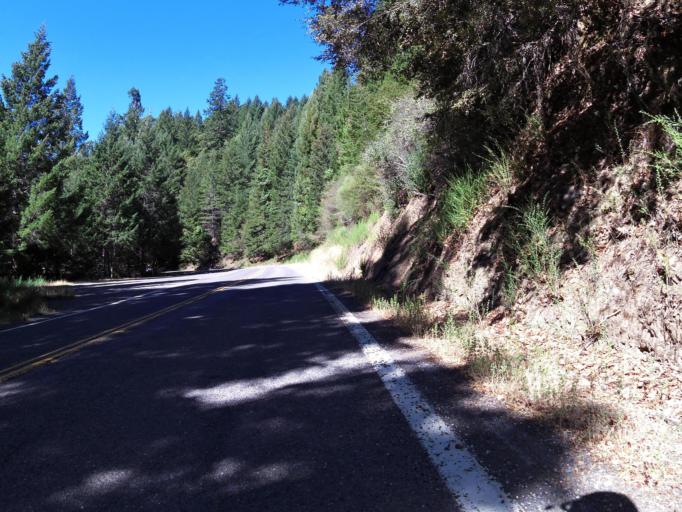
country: US
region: California
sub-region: Humboldt County
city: Redway
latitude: 39.8495
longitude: -123.7371
